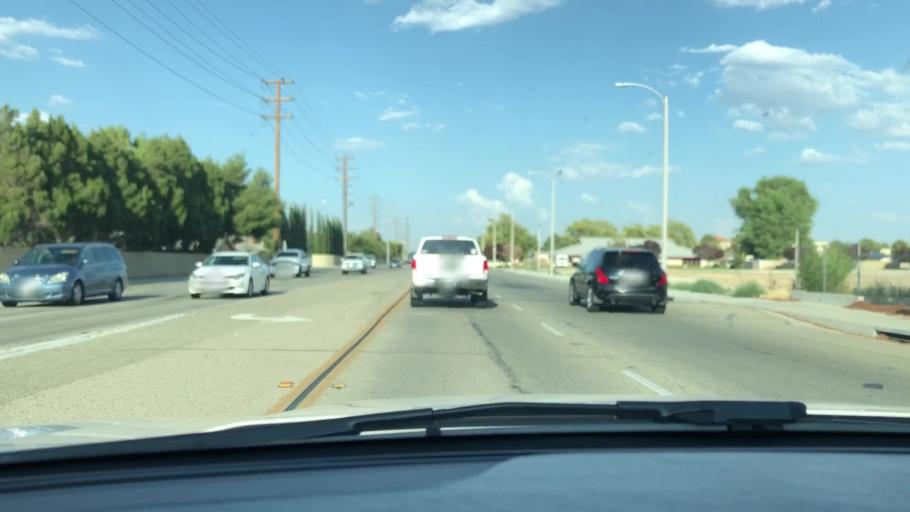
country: US
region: California
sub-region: Los Angeles County
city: Lancaster
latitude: 34.6749
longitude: -118.1717
